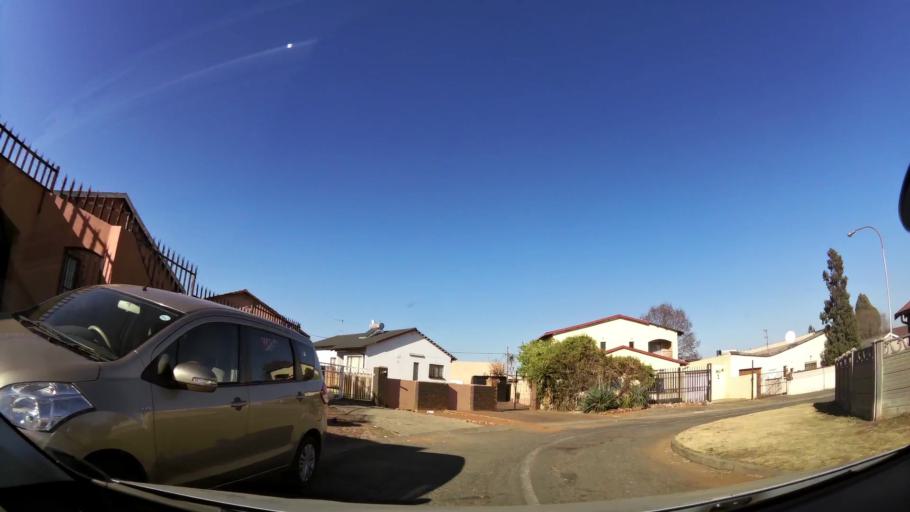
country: ZA
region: Gauteng
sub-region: City of Johannesburg Metropolitan Municipality
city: Johannesburg
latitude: -26.2052
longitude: 27.9596
